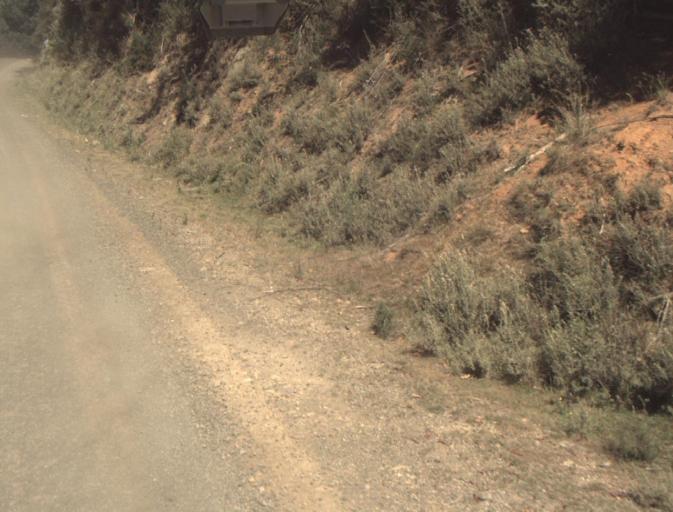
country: AU
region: Tasmania
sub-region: Dorset
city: Scottsdale
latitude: -41.3749
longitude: 147.4753
